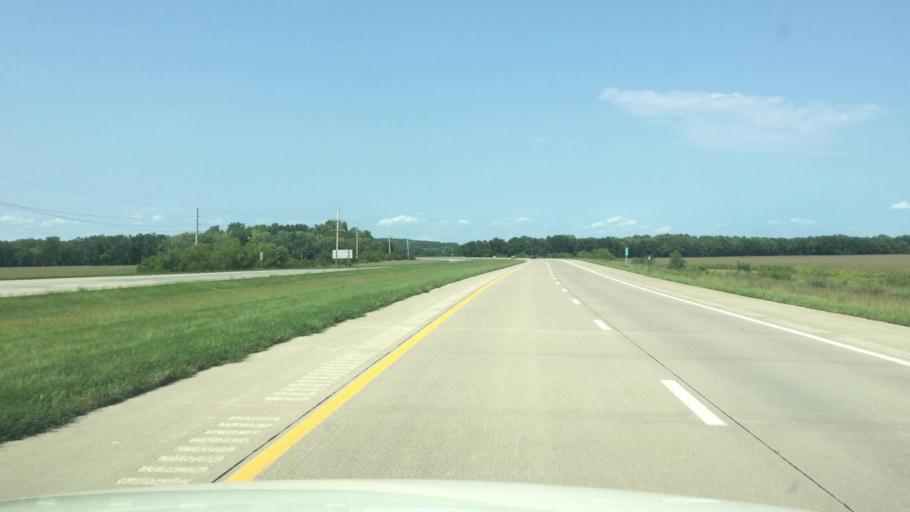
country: US
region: Kansas
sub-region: Linn County
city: Pleasanton
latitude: 38.2293
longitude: -94.6946
